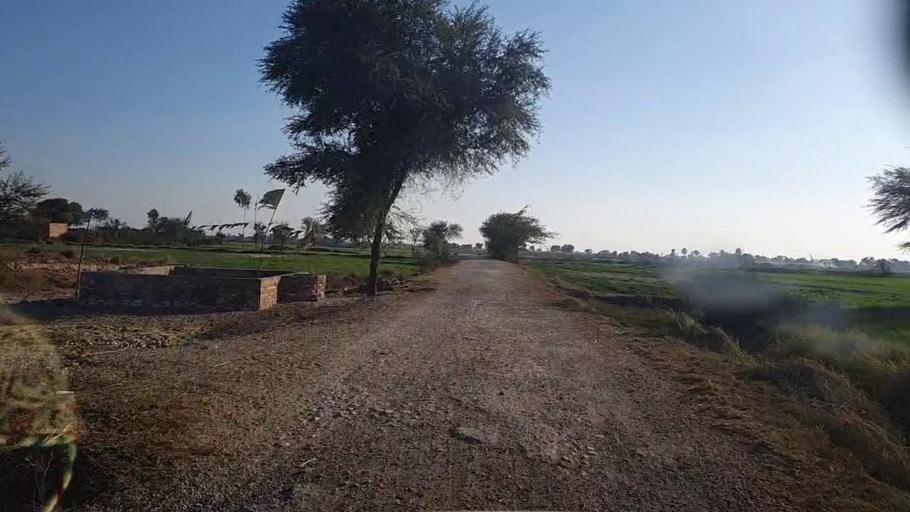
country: PK
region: Sindh
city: Khairpur
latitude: 28.0200
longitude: 69.7107
